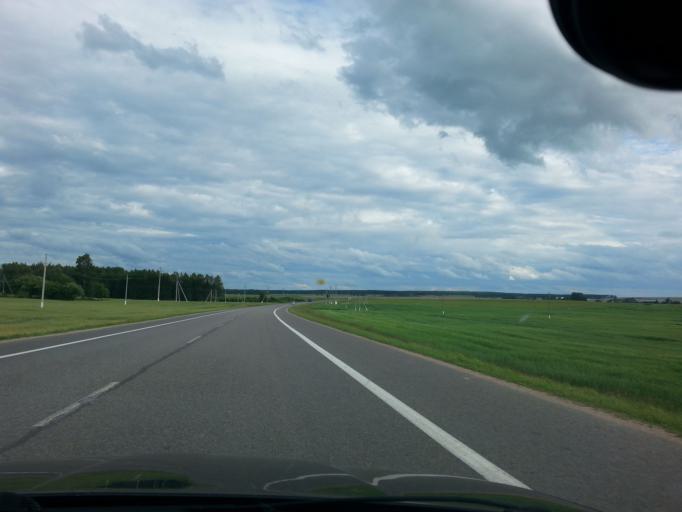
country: BY
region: Grodnenskaya
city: Astravyets
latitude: 54.7438
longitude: 26.0848
